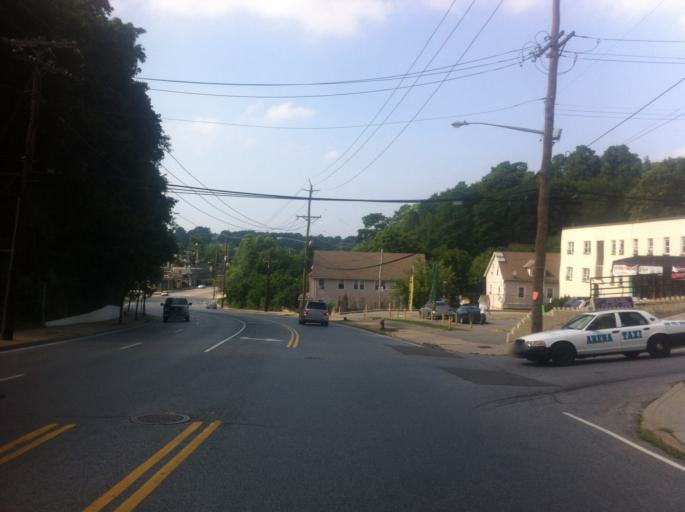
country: US
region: New York
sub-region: Nassau County
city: Glen Cove
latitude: 40.8552
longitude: -73.6343
